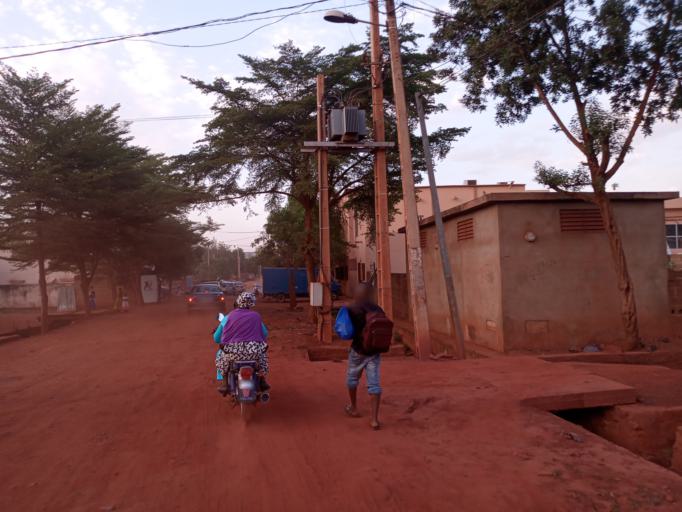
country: ML
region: Bamako
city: Bamako
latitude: 12.5820
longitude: -8.0222
